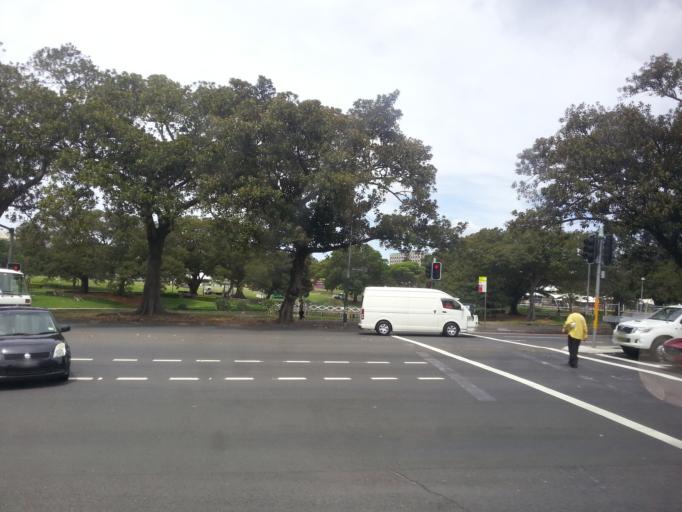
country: AU
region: New South Wales
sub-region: City of Sydney
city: Chippendale
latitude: -33.8845
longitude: 151.1929
